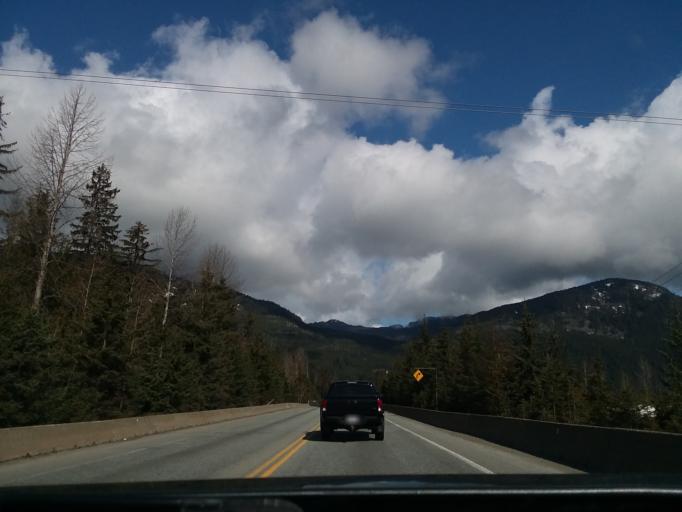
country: CA
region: British Columbia
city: Whistler
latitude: 50.1373
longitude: -122.9543
